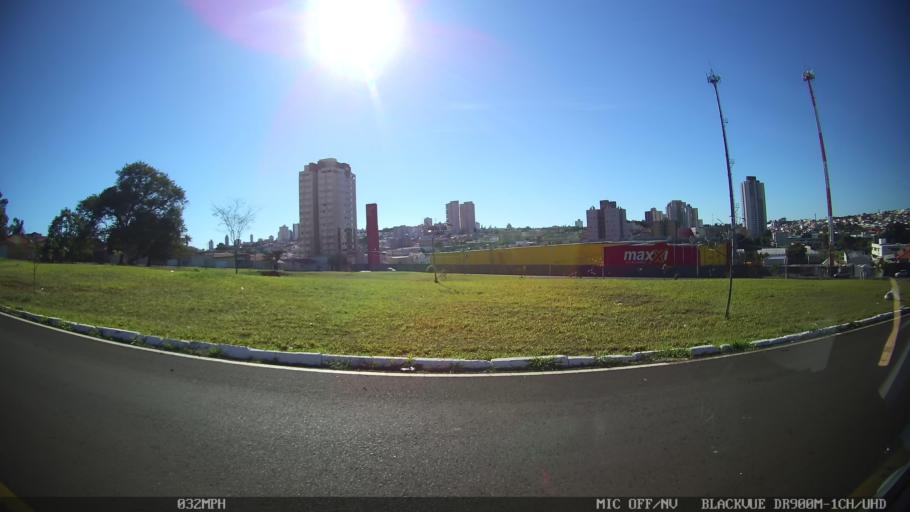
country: BR
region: Sao Paulo
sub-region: Franca
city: Franca
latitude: -20.5510
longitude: -47.4116
